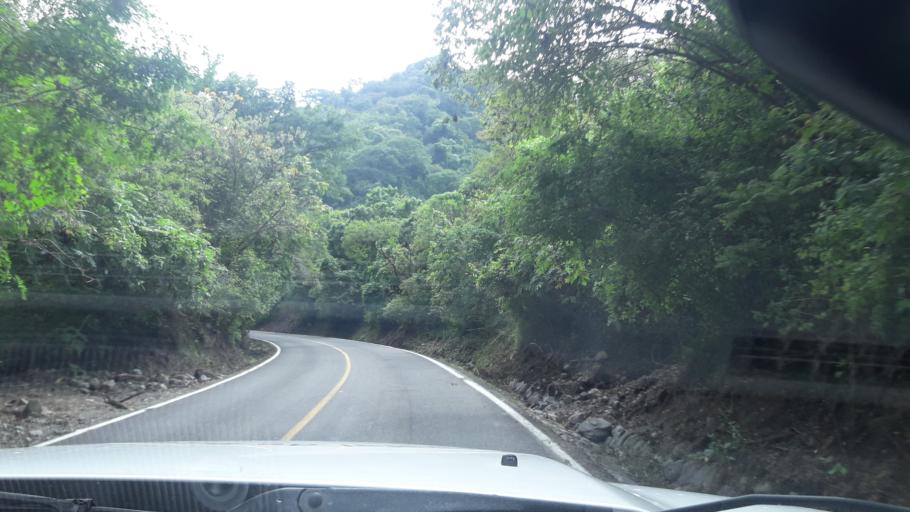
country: MX
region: Colima
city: Suchitlan
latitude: 19.4416
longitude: -103.7154
